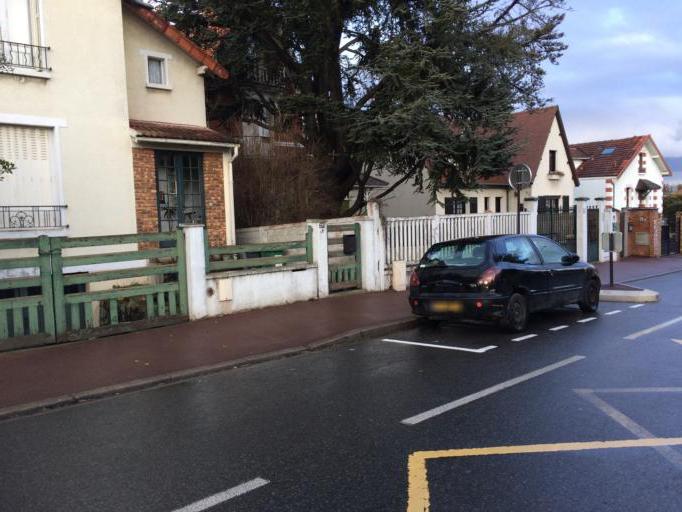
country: FR
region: Ile-de-France
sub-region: Departement des Hauts-de-Seine
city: Antony
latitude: 48.7387
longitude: 2.2939
